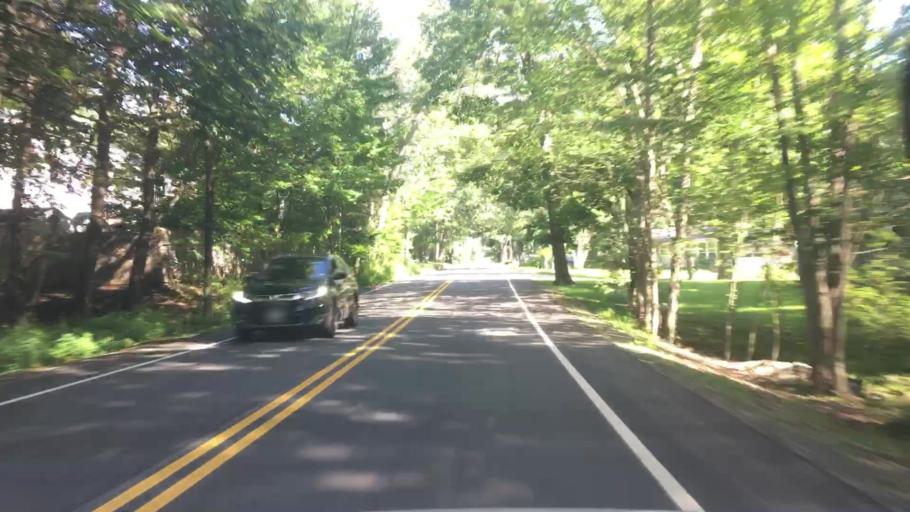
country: US
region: New Hampshire
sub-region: Strafford County
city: Dover
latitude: 43.1627
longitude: -70.8792
